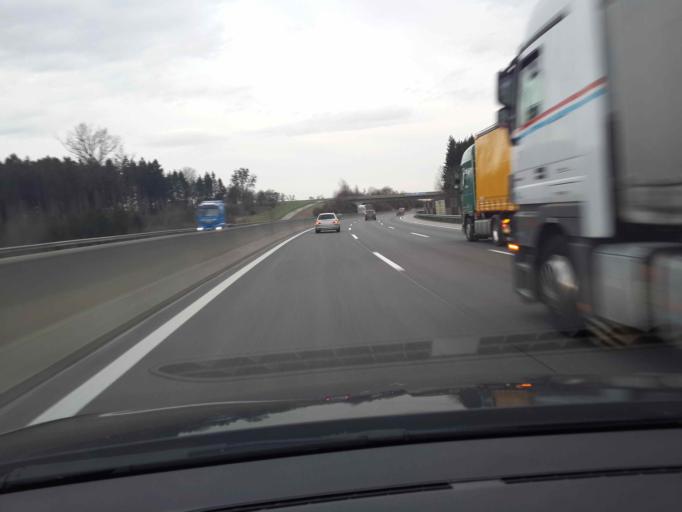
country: AT
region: Lower Austria
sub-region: Politischer Bezirk Amstetten
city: Strengberg
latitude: 48.1156
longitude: 14.6290
